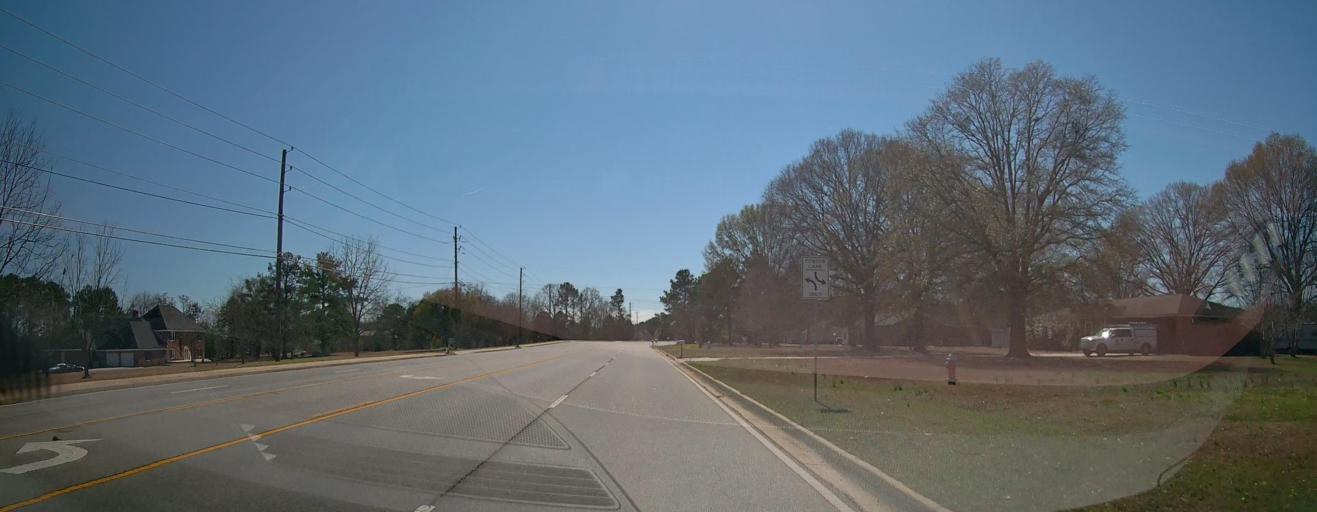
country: US
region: Georgia
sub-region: Houston County
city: Perry
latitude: 32.5119
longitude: -83.6474
